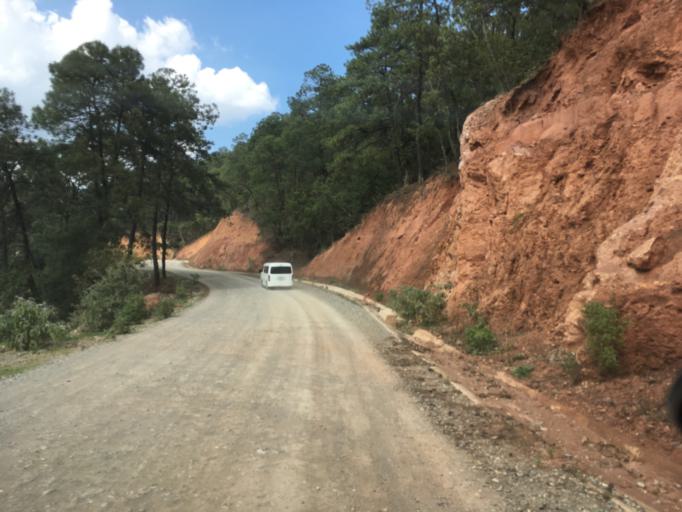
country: MX
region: Oaxaca
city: Santiago Tilantongo
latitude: 17.2043
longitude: -97.2799
